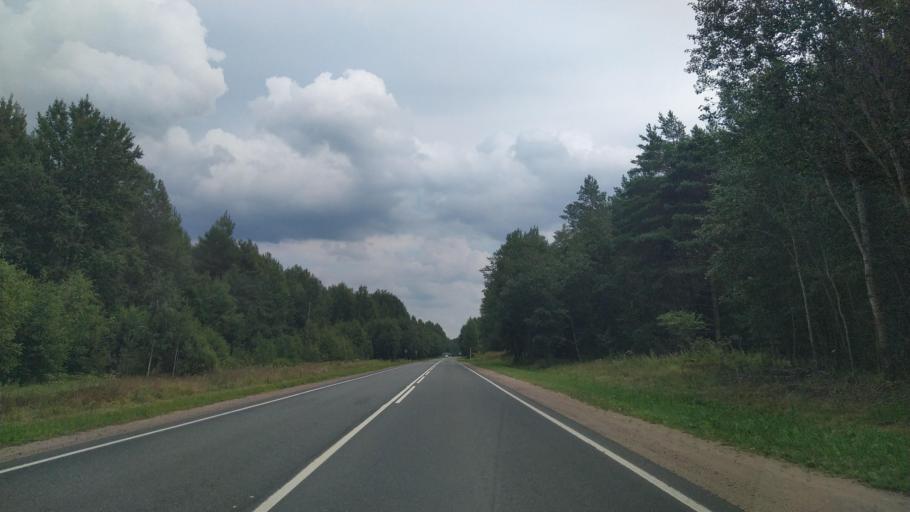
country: RU
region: Pskov
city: Pskov
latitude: 57.8334
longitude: 28.5205
